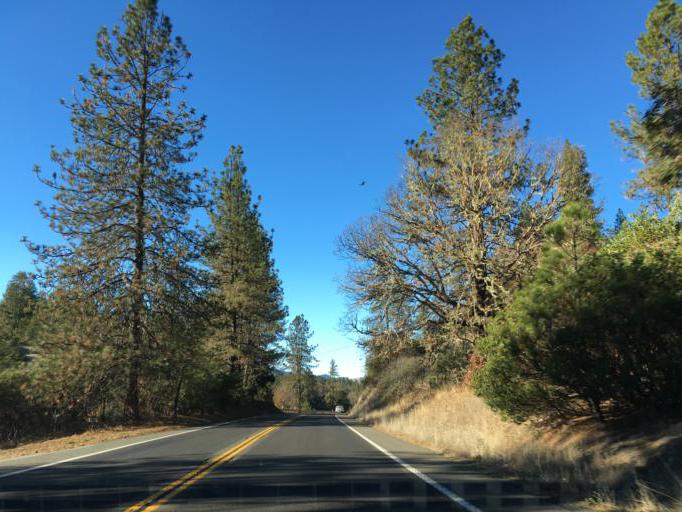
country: US
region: California
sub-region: Mendocino County
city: Laytonville
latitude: 39.7324
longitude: -123.5110
